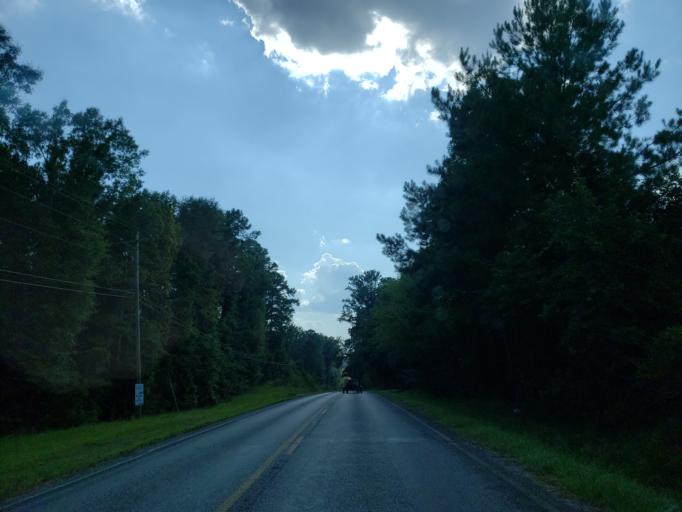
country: US
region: Mississippi
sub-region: Jones County
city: Sharon
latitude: 31.9197
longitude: -89.0245
